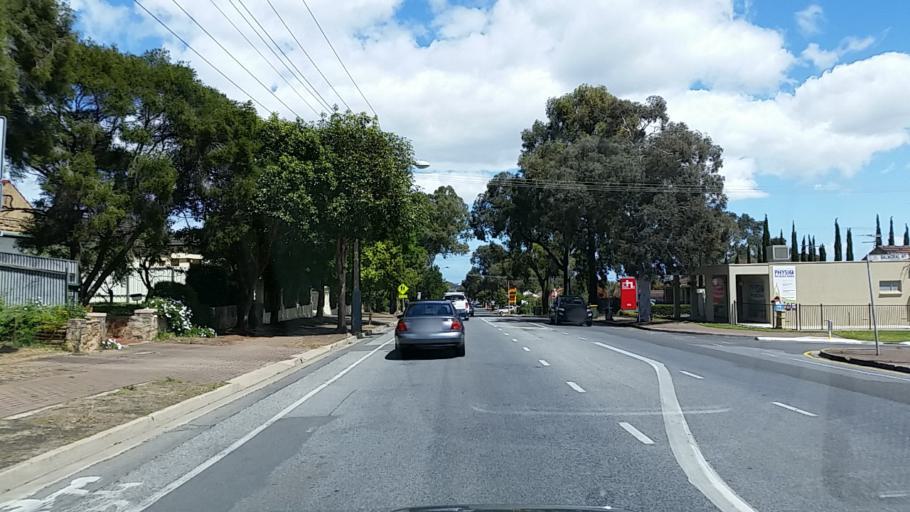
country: AU
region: South Australia
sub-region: Burnside
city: Wattle Park
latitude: -34.9133
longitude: 138.6714
